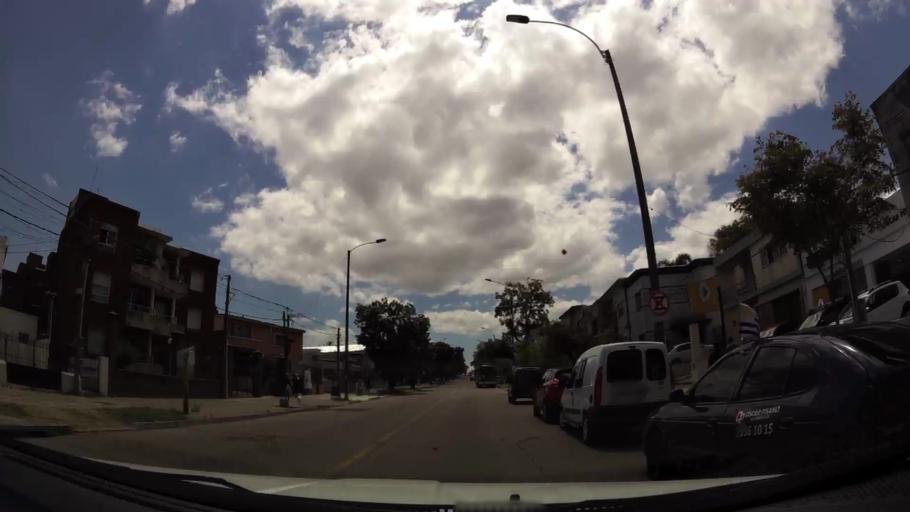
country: UY
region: Montevideo
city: Montevideo
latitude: -34.8457
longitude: -56.2028
